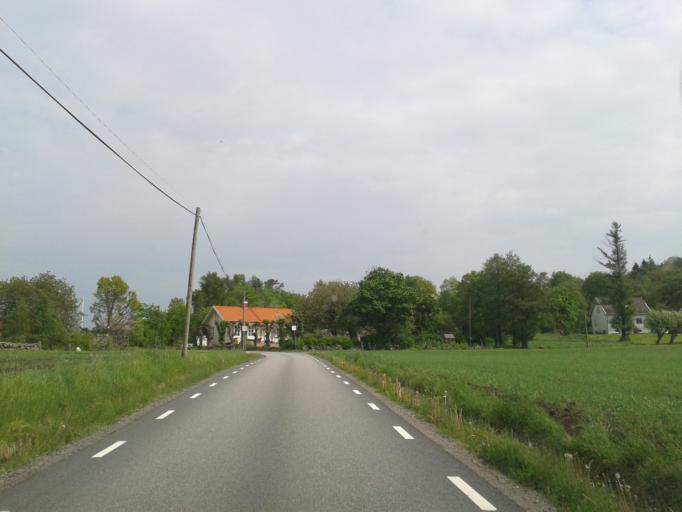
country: SE
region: Vaestra Goetaland
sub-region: Kungalvs Kommun
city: Kungalv
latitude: 57.9182
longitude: 11.9520
